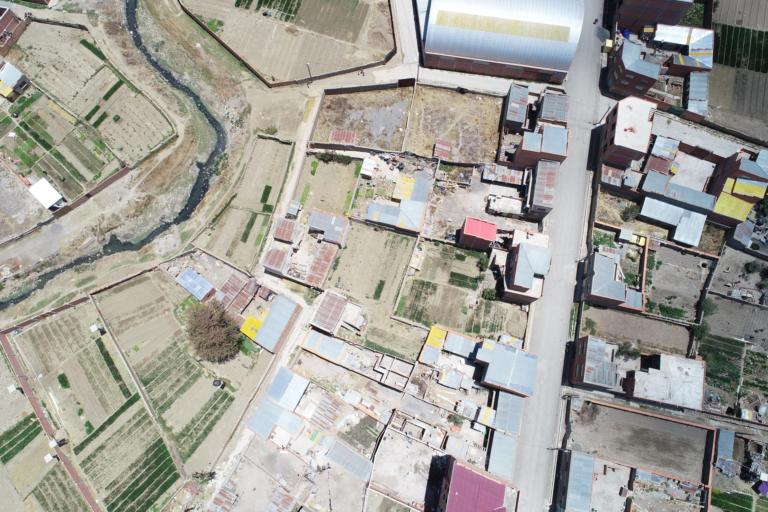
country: BO
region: La Paz
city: Achacachi
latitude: -16.0405
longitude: -68.6891
